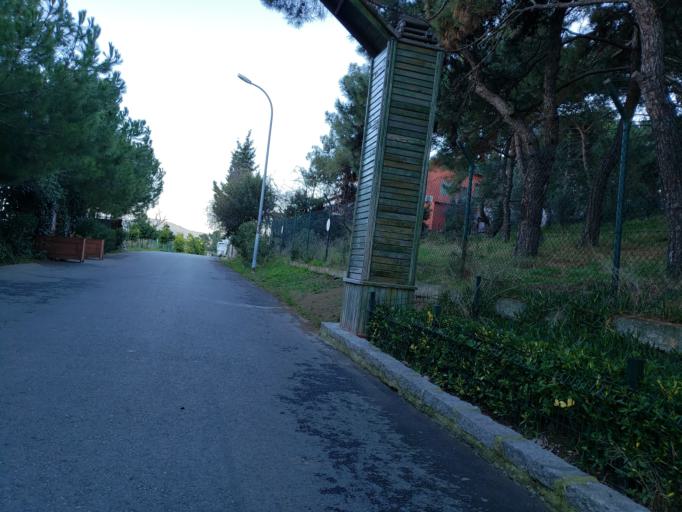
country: TR
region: Istanbul
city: Adalan
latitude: 40.8835
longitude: 29.0980
